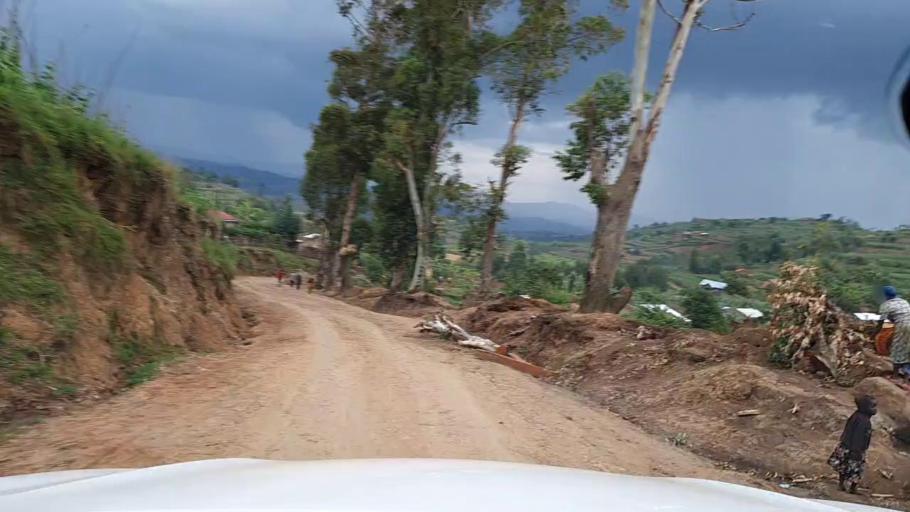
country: BI
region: Kayanza
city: Kayanza
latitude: -2.7924
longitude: 29.5182
